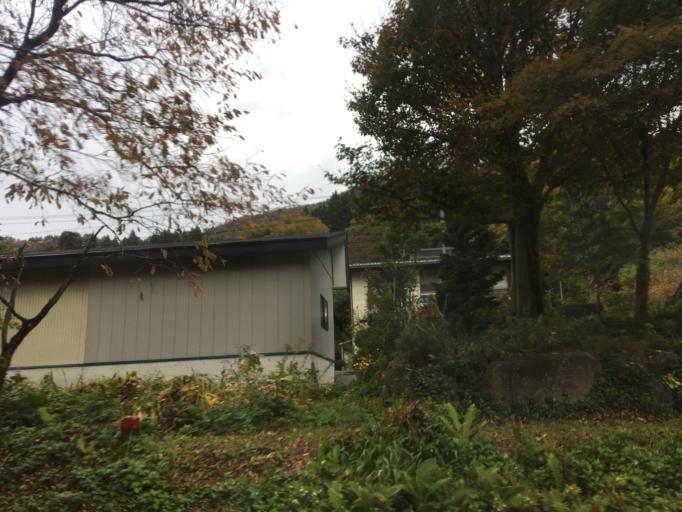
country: JP
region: Yamagata
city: Nagai
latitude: 38.0502
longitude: 139.8247
